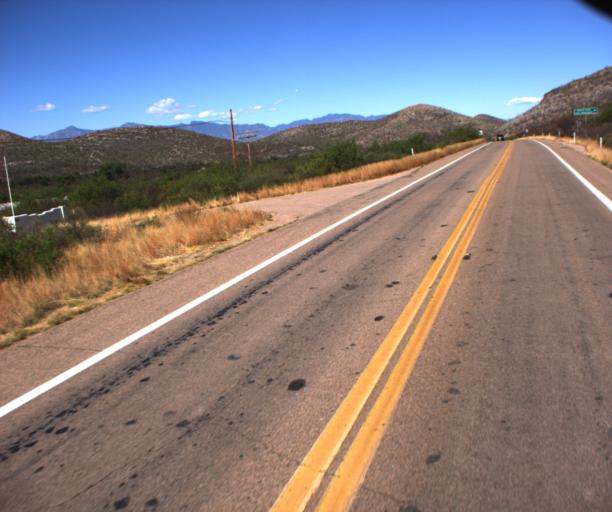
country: US
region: Arizona
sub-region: Cochise County
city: Bisbee
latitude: 31.5169
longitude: -110.0209
